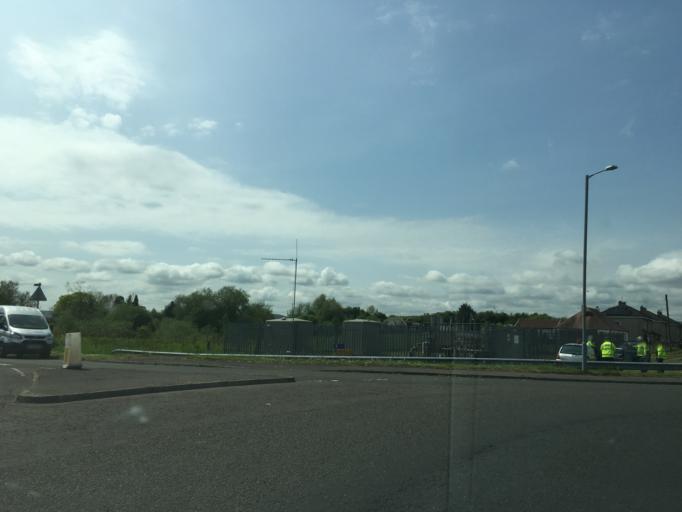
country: GB
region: Scotland
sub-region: Stirling
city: Bannockburn
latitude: 56.1122
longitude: -3.9094
